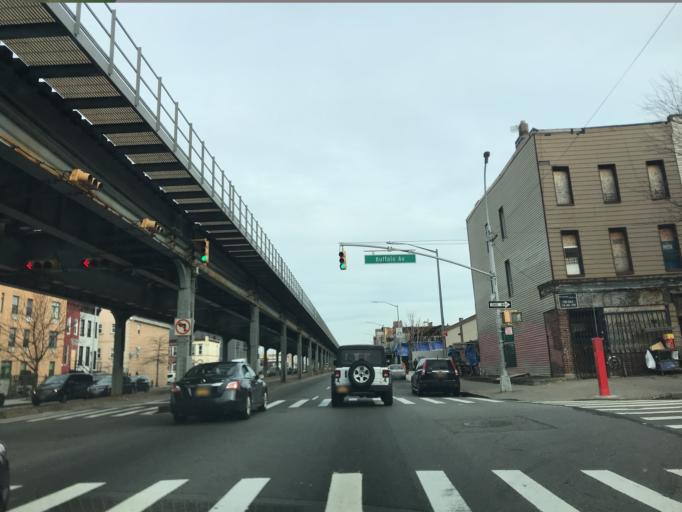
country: US
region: New York
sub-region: Kings County
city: Brooklyn
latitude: 40.6770
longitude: -73.9251
